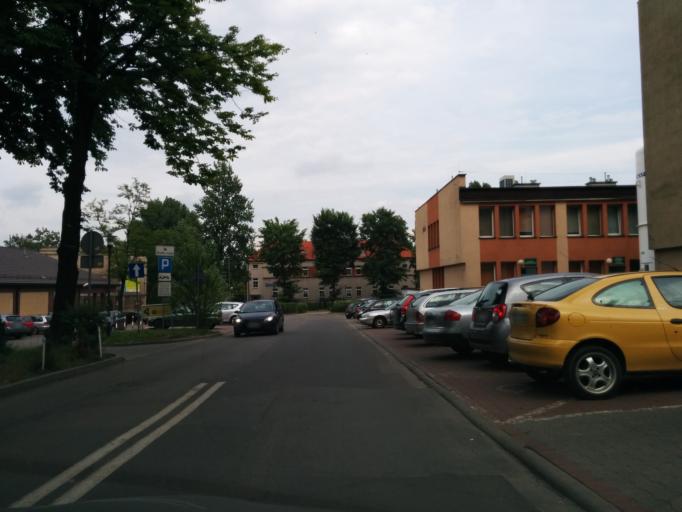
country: PL
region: Silesian Voivodeship
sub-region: Ruda Slaska
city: Ruda Slaska
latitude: 50.2887
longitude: 18.8752
